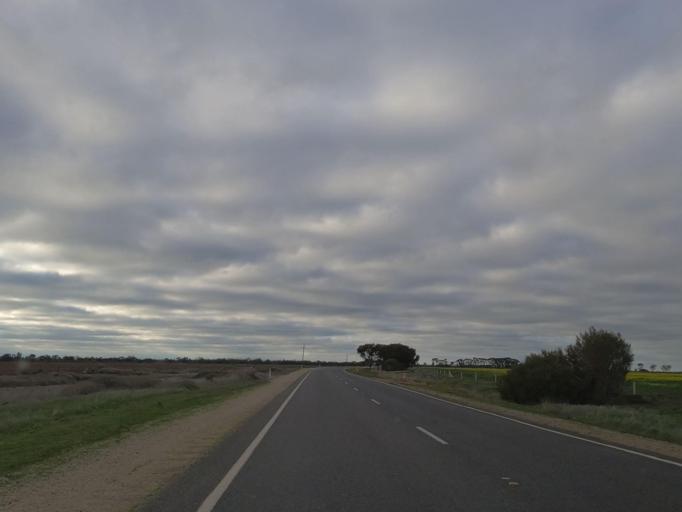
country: AU
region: Victoria
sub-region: Swan Hill
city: Swan Hill
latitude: -35.8296
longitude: 143.9448
